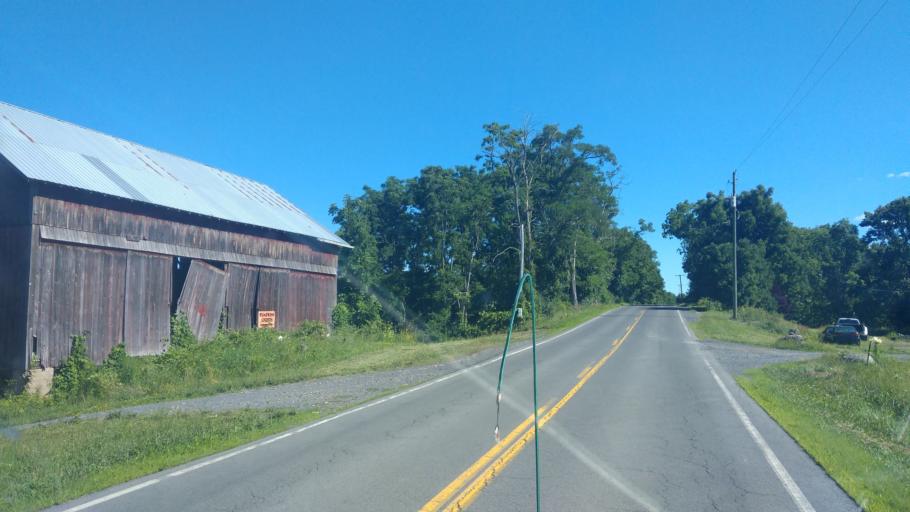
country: US
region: New York
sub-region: Seneca County
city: Seneca Falls
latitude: 42.9846
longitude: -76.8001
